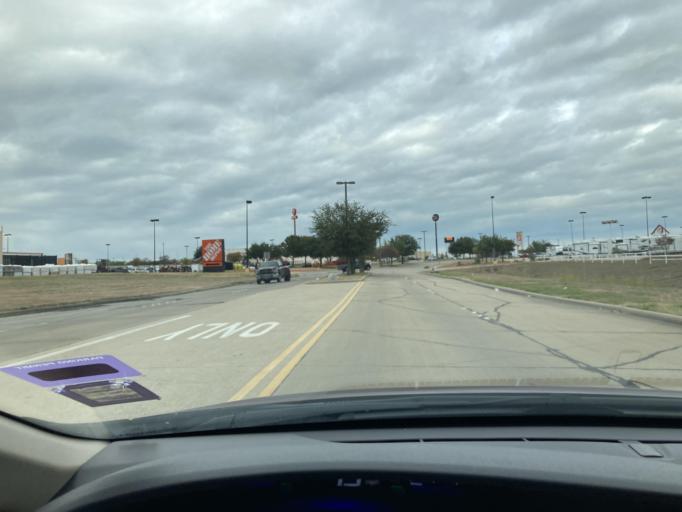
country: US
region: Texas
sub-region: Navarro County
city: Corsicana
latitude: 32.0654
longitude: -96.4477
